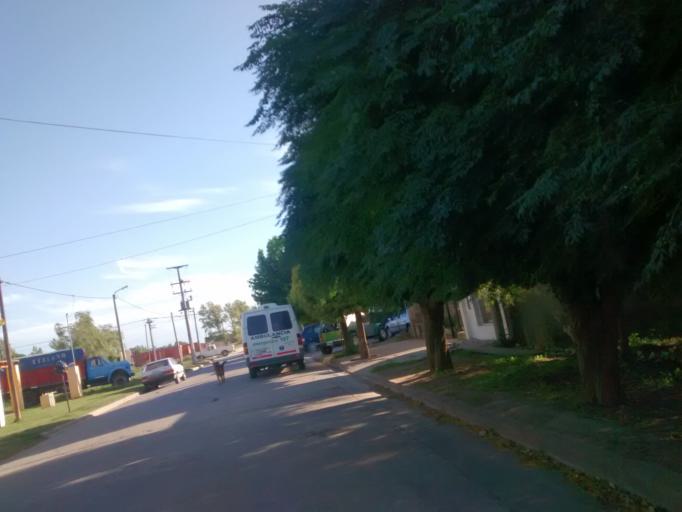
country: AR
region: Buenos Aires
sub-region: Partido de Loberia
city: Loberia
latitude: -38.1701
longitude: -58.7819
